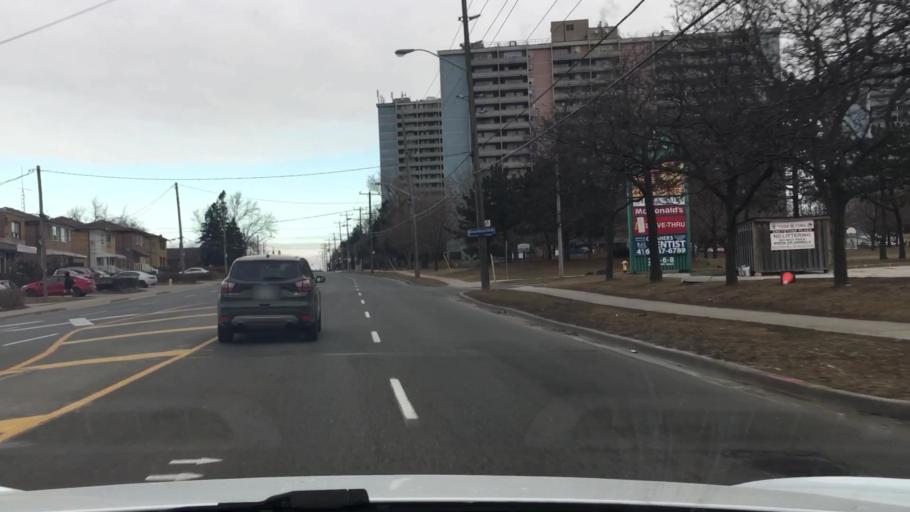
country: CA
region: Ontario
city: Scarborough
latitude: 43.7255
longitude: -79.2535
